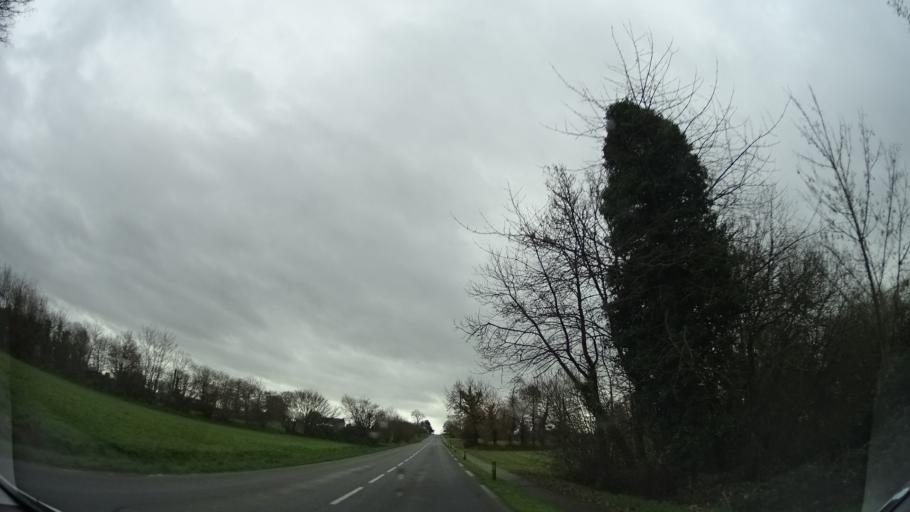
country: FR
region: Brittany
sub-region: Departement des Cotes-d'Armor
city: Lanvallay
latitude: 48.4436
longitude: -2.0196
